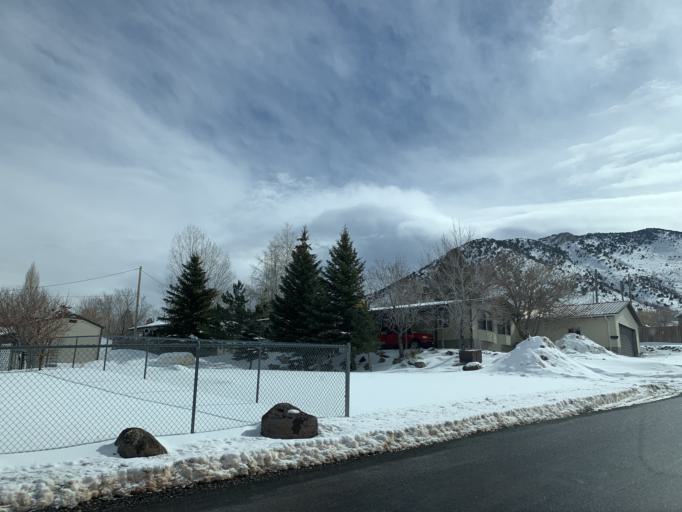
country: US
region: Utah
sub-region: Utah County
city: Genola
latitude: 39.9538
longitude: -112.1180
